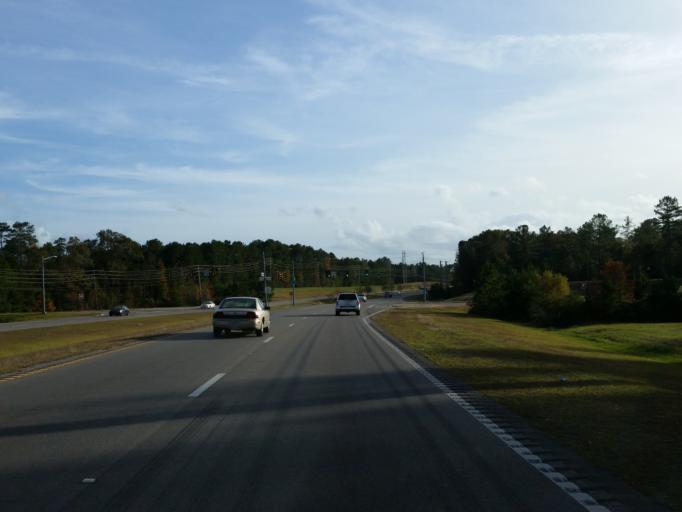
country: US
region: Mississippi
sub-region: Forrest County
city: Hattiesburg
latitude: 31.2902
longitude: -89.3227
